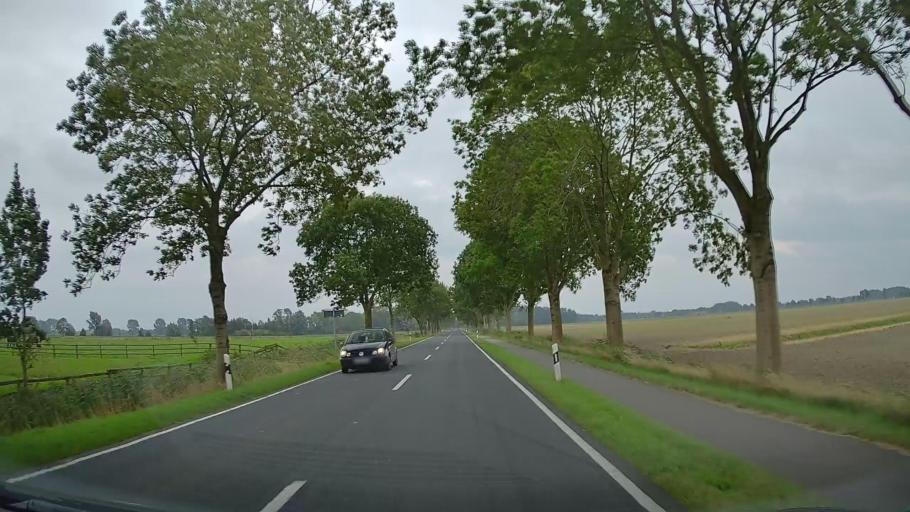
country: DE
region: Lower Saxony
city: Wischhafen
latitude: 53.8070
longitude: 9.3110
